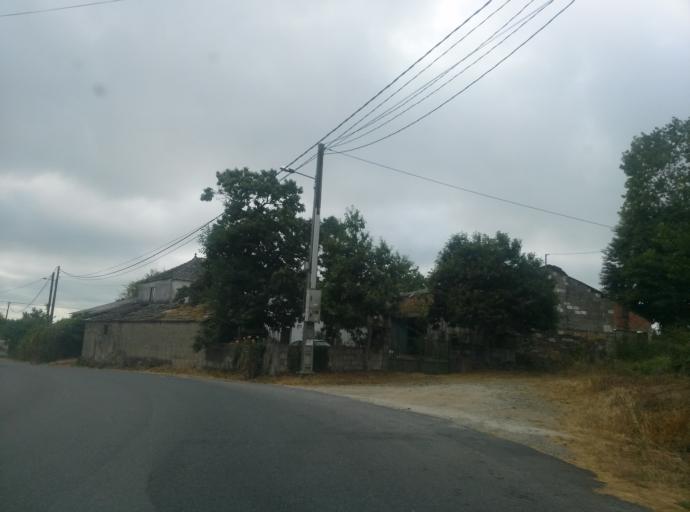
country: ES
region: Galicia
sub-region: Provincia de Lugo
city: Lugo
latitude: 43.0576
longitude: -7.5665
